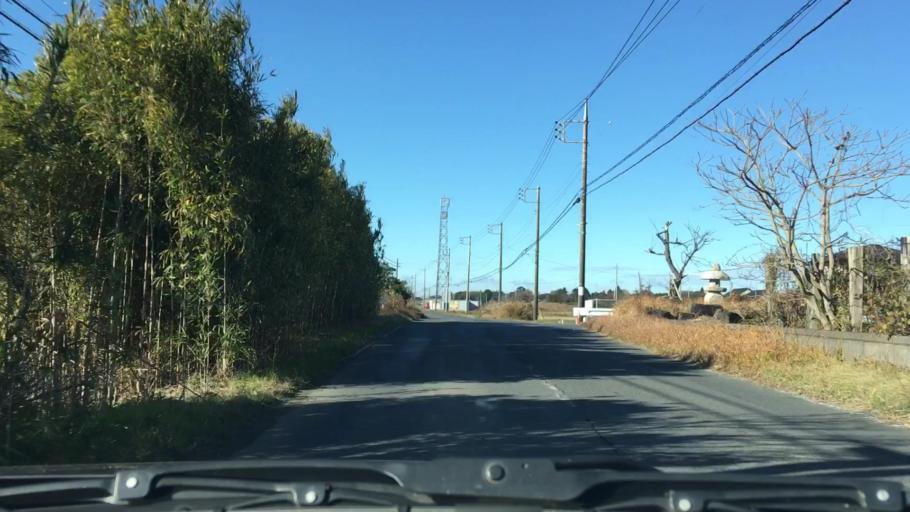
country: JP
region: Chiba
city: Omigawa
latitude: 35.8644
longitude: 140.6757
